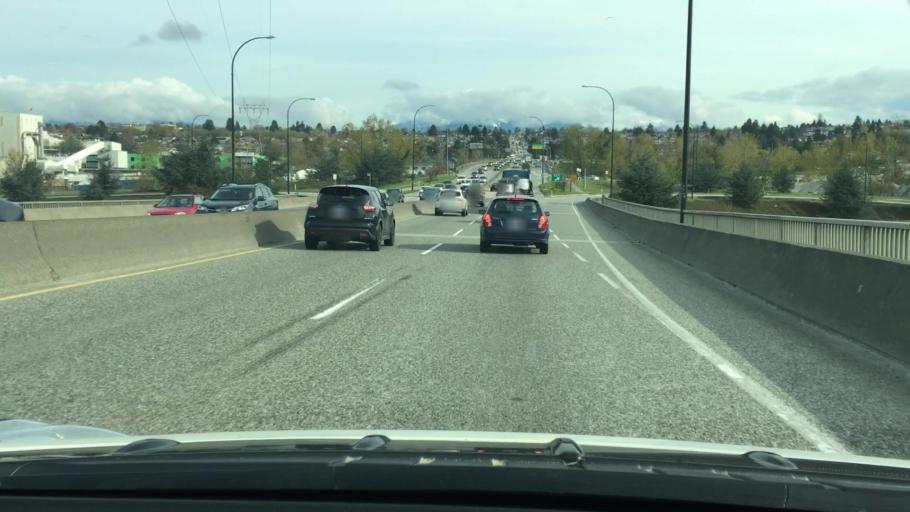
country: CA
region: British Columbia
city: Vancouver
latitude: 49.2049
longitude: -123.0774
